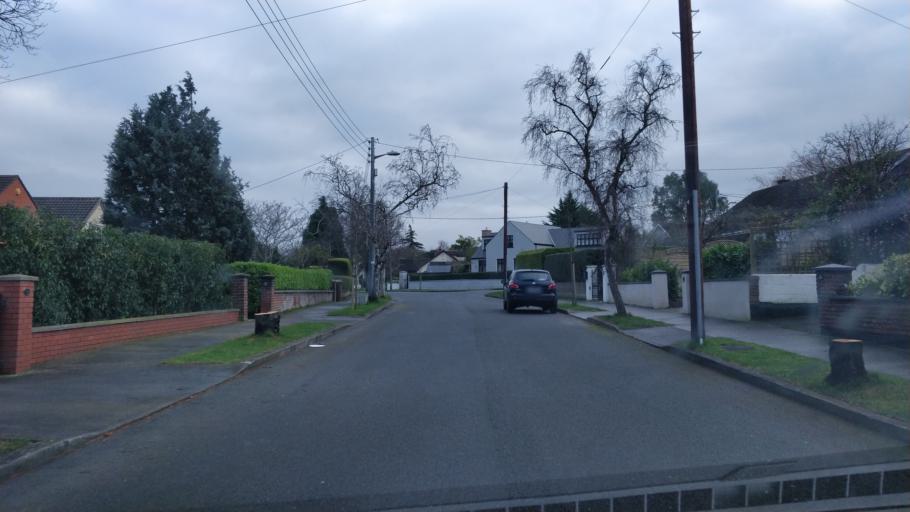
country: IE
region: Leinster
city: Foxrock
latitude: 53.2809
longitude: -6.1786
